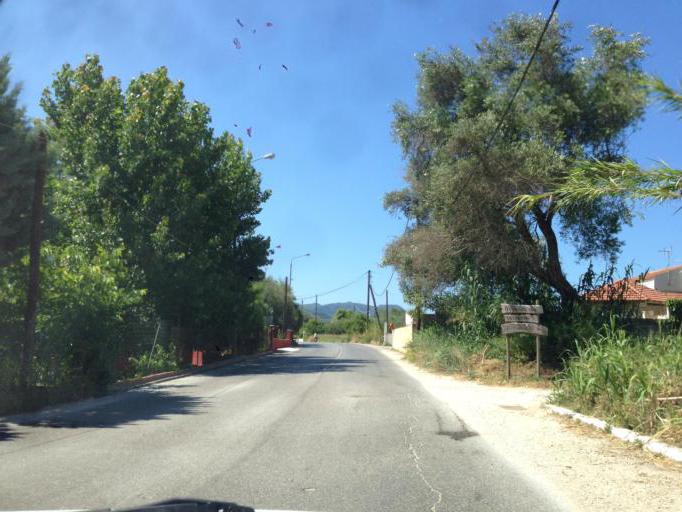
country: GR
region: Ionian Islands
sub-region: Nomos Kerkyras
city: Agios Georgis
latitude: 39.7577
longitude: 19.7192
